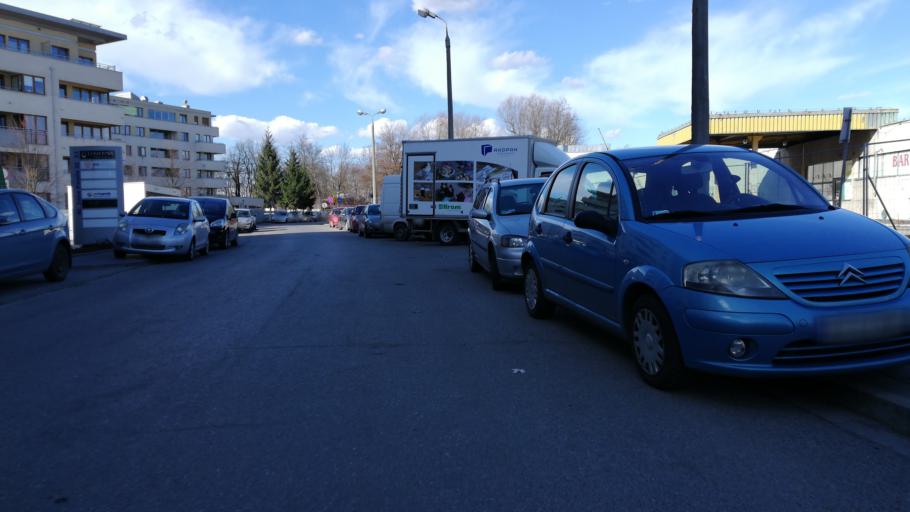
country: PL
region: Lesser Poland Voivodeship
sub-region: Krakow
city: Krakow
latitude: 50.0745
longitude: 19.9944
